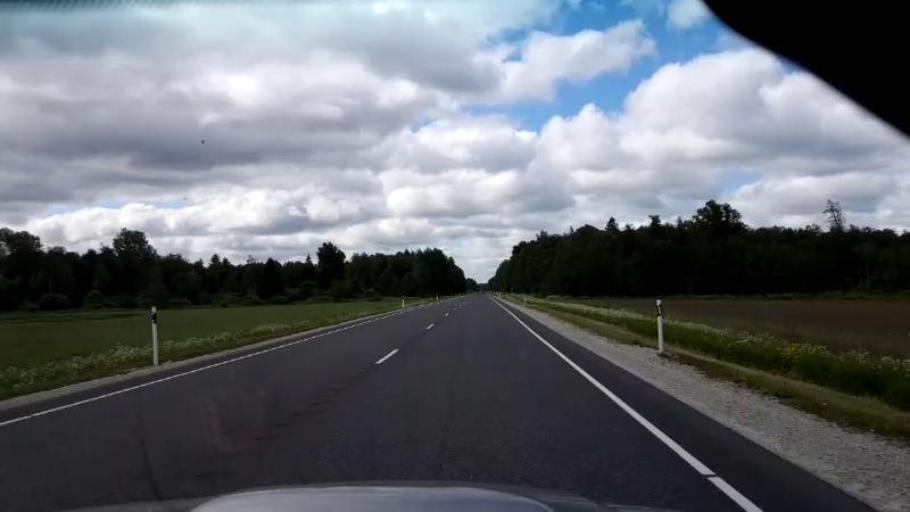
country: EE
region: Raplamaa
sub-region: Maerjamaa vald
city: Marjamaa
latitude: 58.8402
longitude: 24.4237
